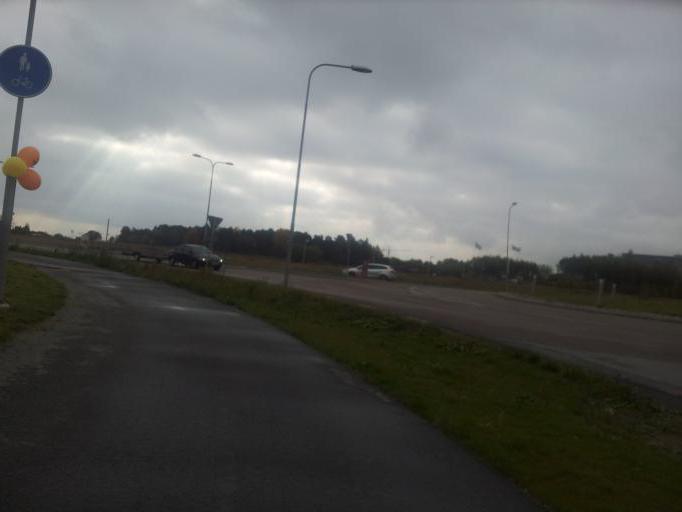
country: SE
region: Uppsala
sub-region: Uppsala Kommun
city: Gamla Uppsala
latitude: 59.8853
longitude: 17.6679
